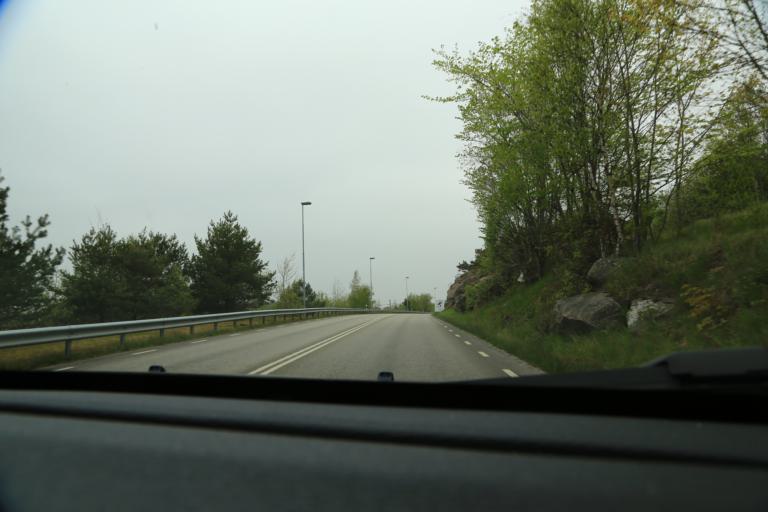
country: SE
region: Halland
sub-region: Varbergs Kommun
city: Varberg
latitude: 57.1703
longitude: 12.2303
